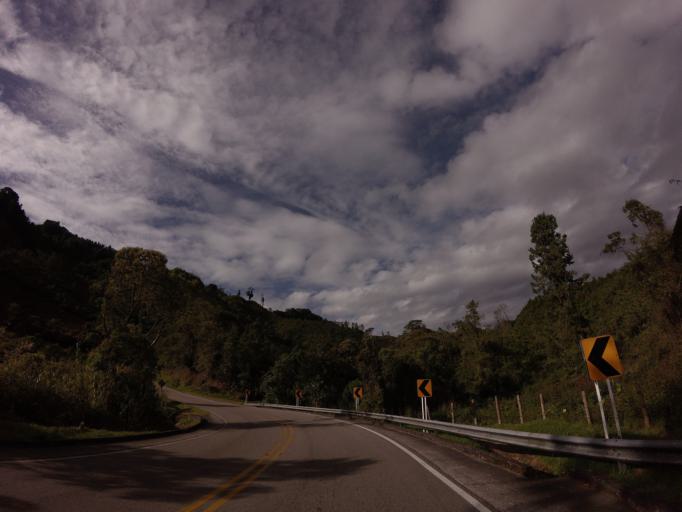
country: CO
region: Tolima
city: Herveo
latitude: 5.1374
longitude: -75.1819
